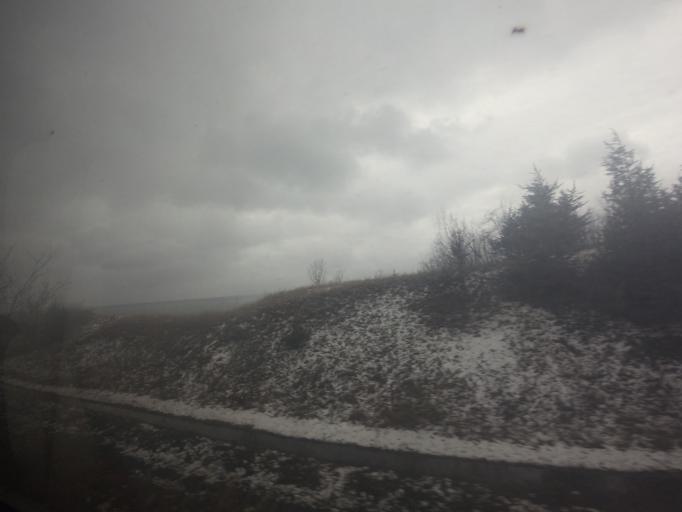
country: CA
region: Ontario
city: Cobourg
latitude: 43.9408
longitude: -78.3100
